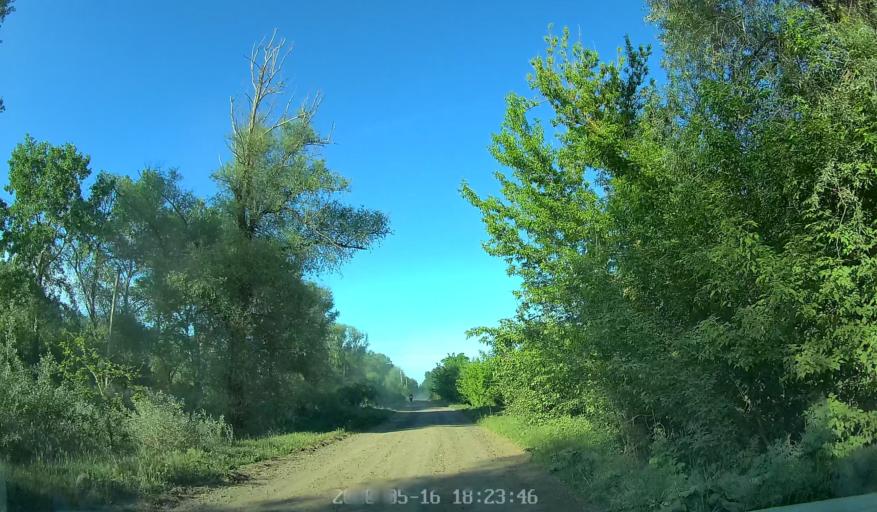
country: MD
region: Telenesti
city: Dnestrovsc
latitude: 46.5426
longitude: 29.9921
